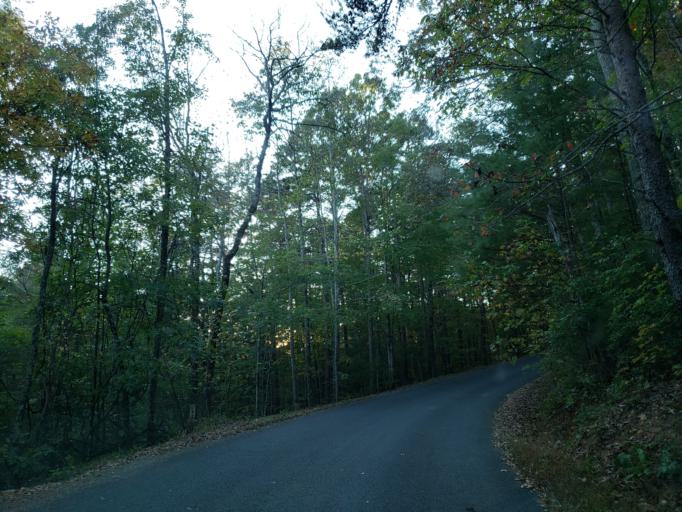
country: US
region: Georgia
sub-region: Gilmer County
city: Ellijay
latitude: 34.6454
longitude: -84.2711
